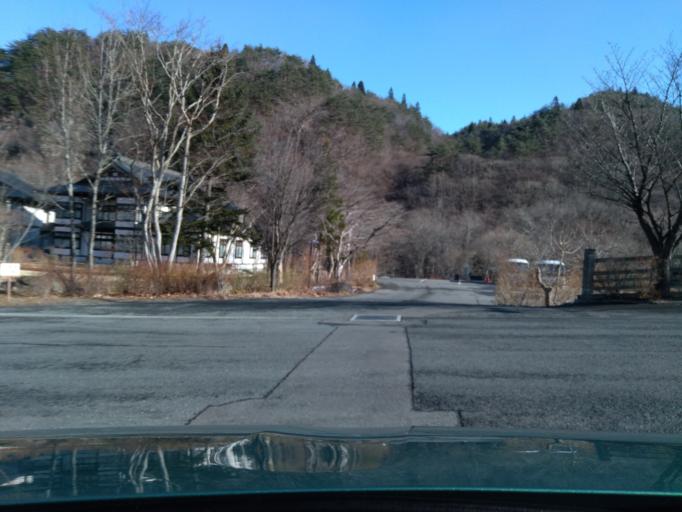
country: JP
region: Iwate
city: Hanamaki
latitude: 39.4520
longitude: 141.0047
